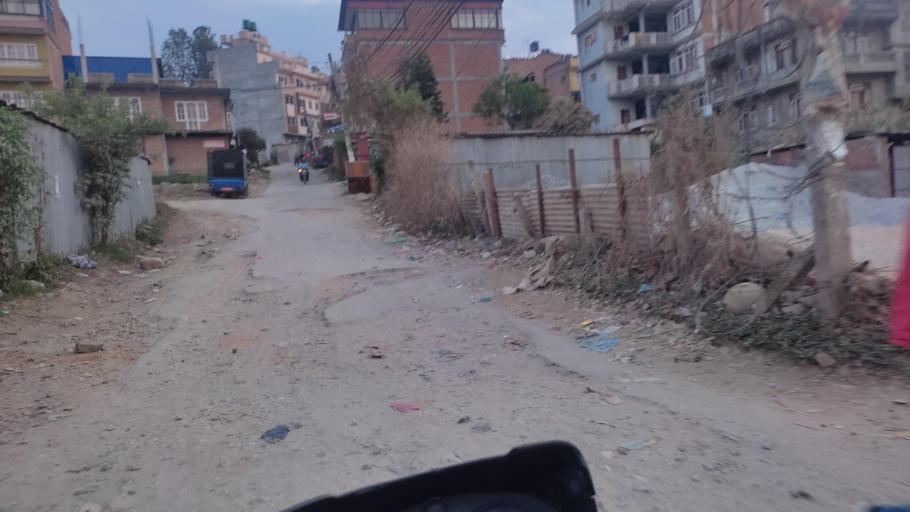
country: NP
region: Central Region
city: Kirtipur
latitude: 27.6729
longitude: 85.2802
